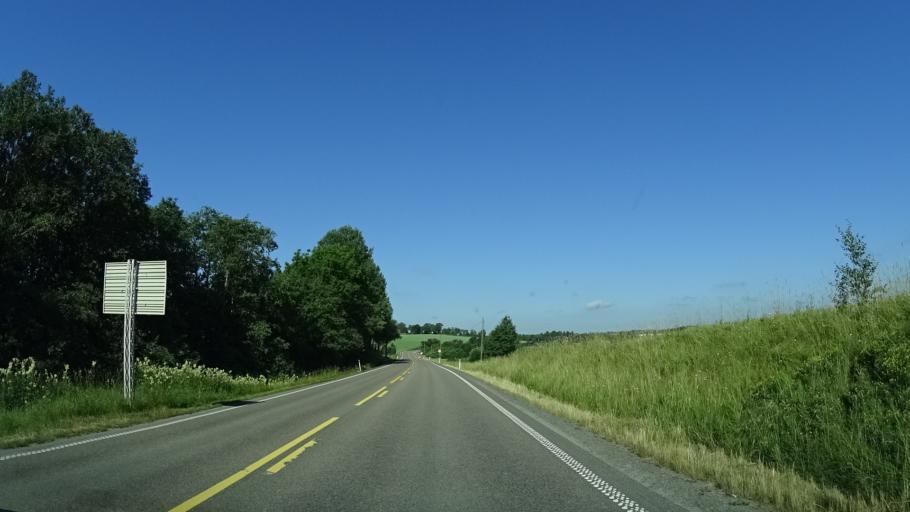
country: NO
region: Akershus
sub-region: Ski
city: Ski
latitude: 59.6848
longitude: 10.8373
